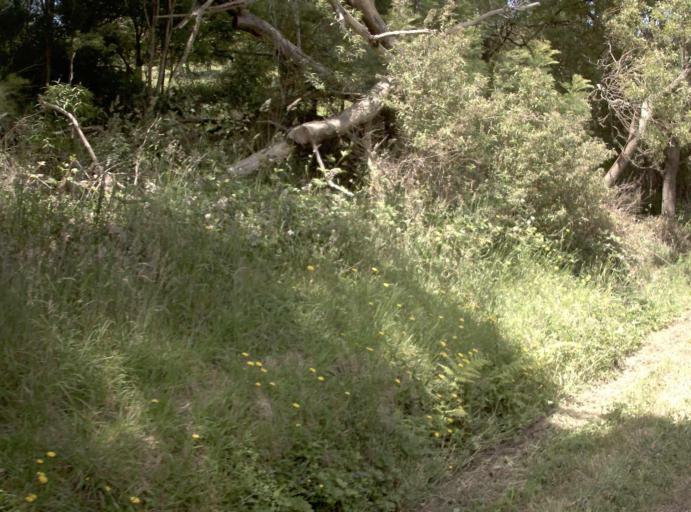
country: AU
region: Victoria
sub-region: Bass Coast
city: North Wonthaggi
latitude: -38.7242
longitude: 146.1211
